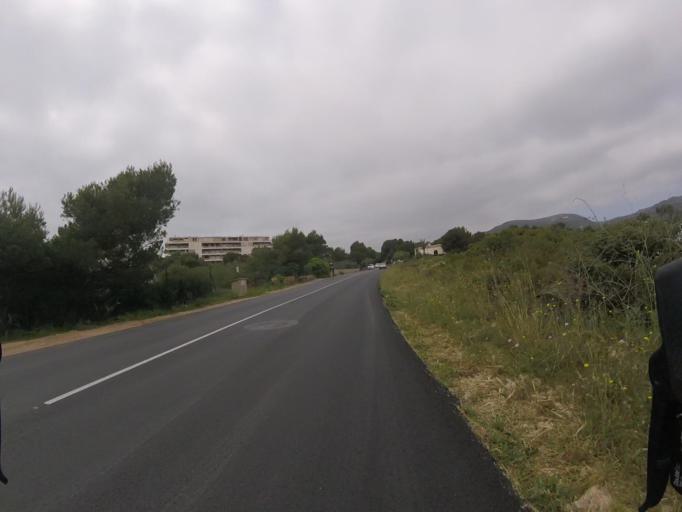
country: ES
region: Valencia
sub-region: Provincia de Castello
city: Peniscola
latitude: 40.3462
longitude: 0.3887
